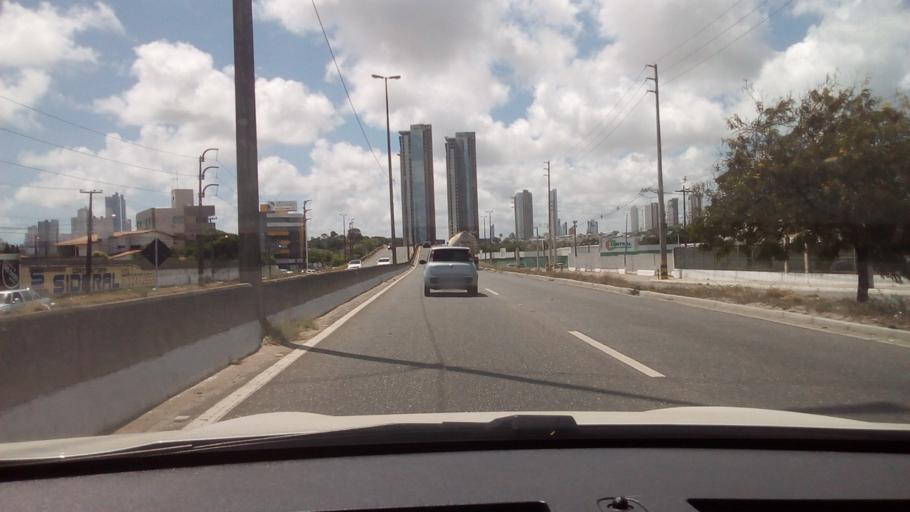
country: BR
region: Paraiba
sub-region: Joao Pessoa
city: Joao Pessoa
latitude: -7.0961
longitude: -34.8480
